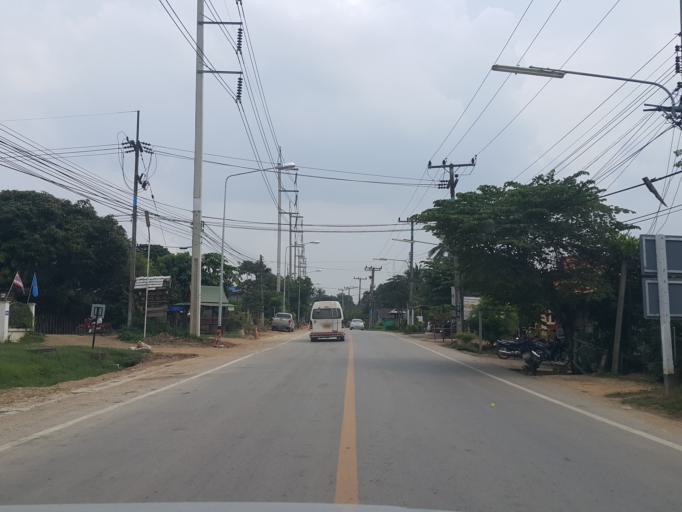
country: TH
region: Chiang Mai
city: Mae Taeng
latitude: 19.0961
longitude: 98.8479
